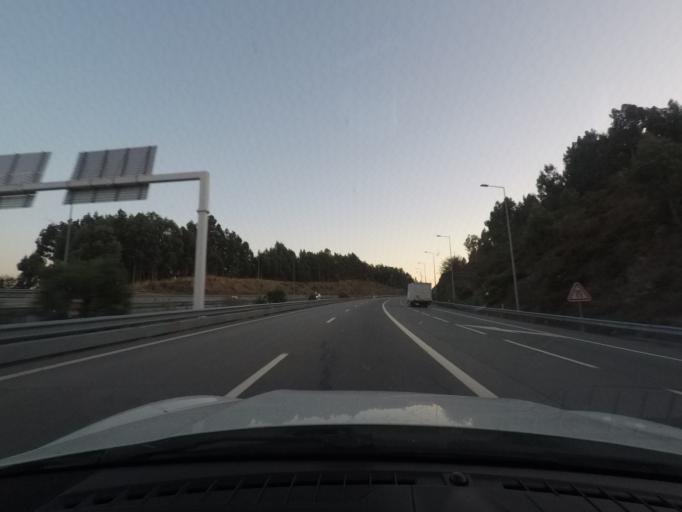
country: PT
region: Porto
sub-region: Felgueiras
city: Margaride
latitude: 41.3266
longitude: -8.2356
